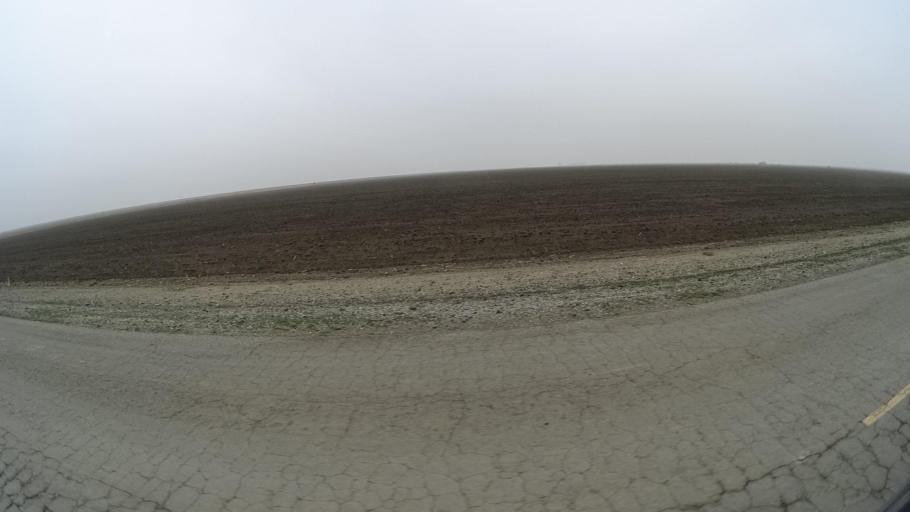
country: US
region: California
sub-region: Kern County
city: Greenfield
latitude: 35.1627
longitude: -119.1990
